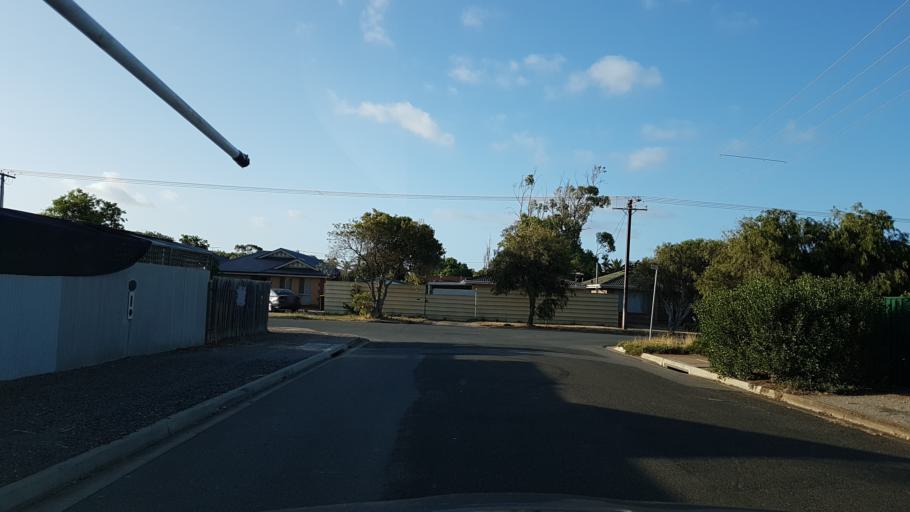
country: AU
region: South Australia
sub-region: Onkaparinga
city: Port Willunga
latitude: -35.2767
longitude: 138.4488
